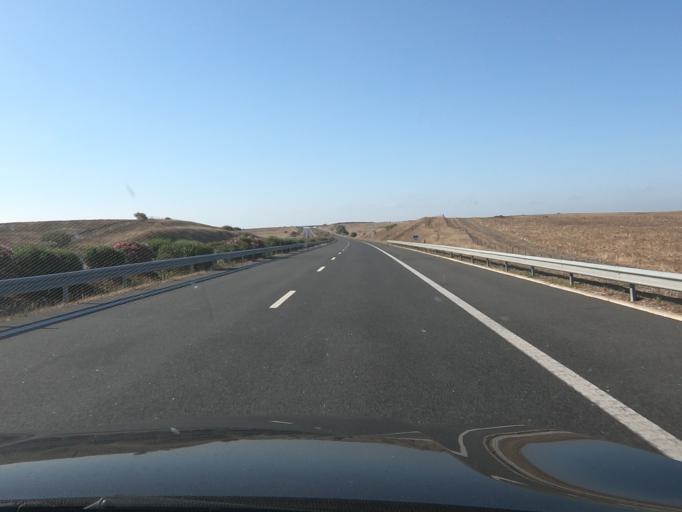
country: PT
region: Beja
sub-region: Aljustrel
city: Aljustrel
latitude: 37.7991
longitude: -8.2256
